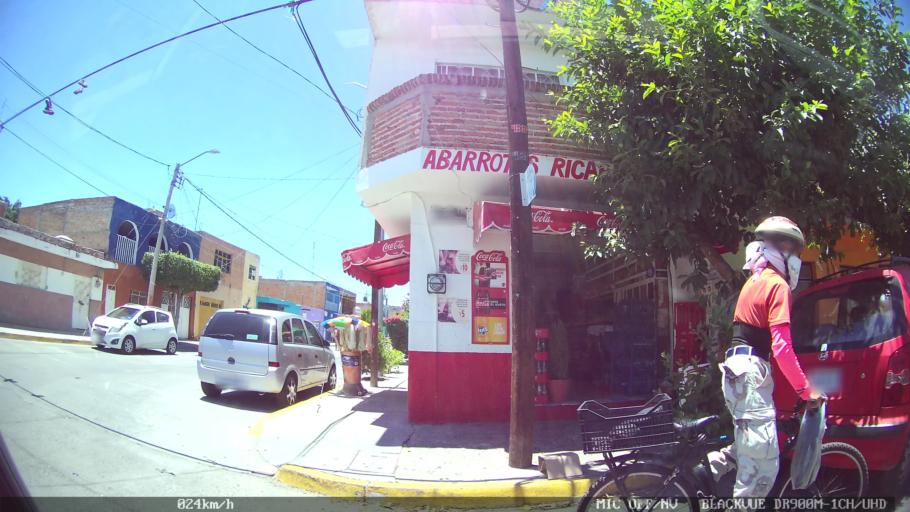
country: MX
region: Jalisco
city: Tlaquepaque
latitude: 20.6712
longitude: -103.2916
